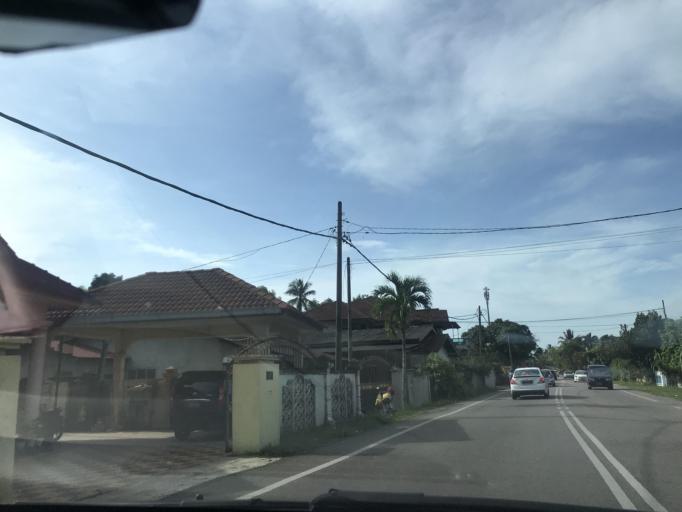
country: MY
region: Kelantan
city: Kota Bharu
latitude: 6.1305
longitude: 102.2016
